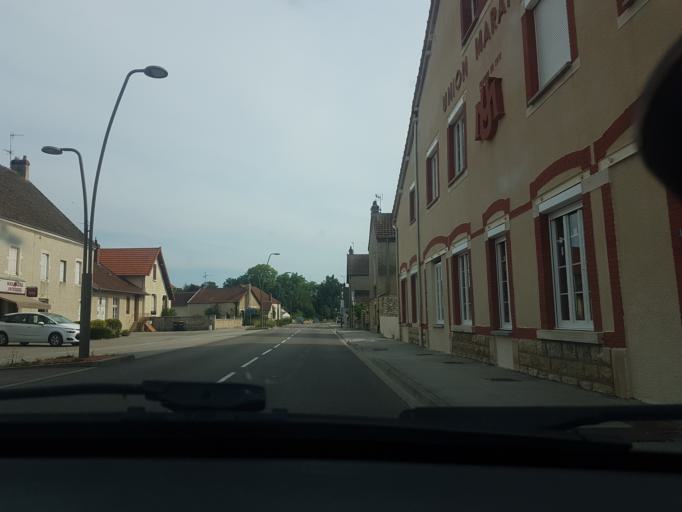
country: FR
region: Bourgogne
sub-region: Departement de Saone-et-Loire
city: Saint-Marcel
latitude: 46.7699
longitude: 4.8936
